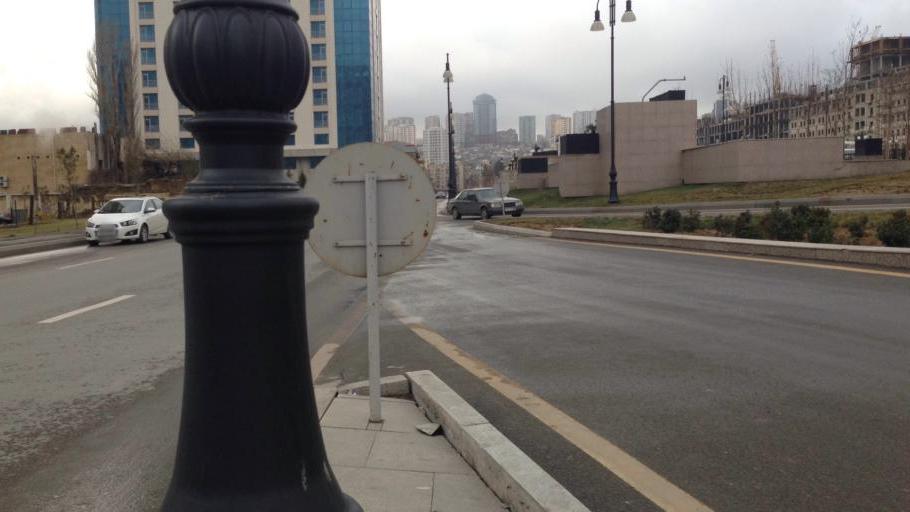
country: AZ
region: Baki
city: Badamdar
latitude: 40.3764
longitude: 49.8394
